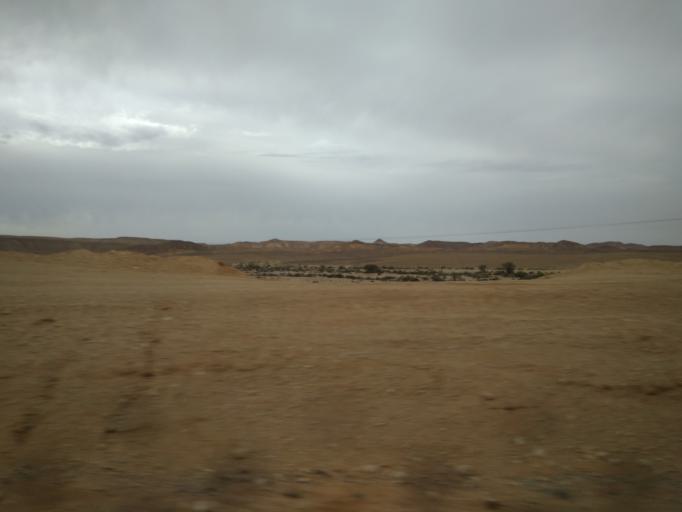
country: IL
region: Southern District
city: Eilat
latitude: 29.8662
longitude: 34.8504
